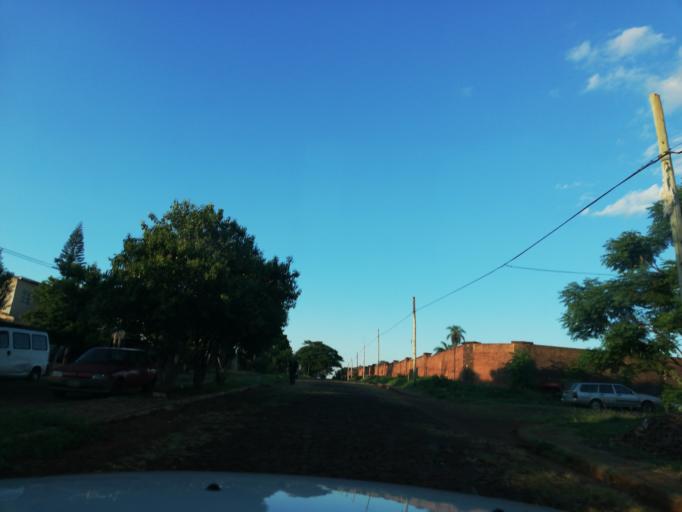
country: AR
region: Misiones
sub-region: Departamento de Capital
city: Posadas
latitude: -27.3842
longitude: -55.9492
